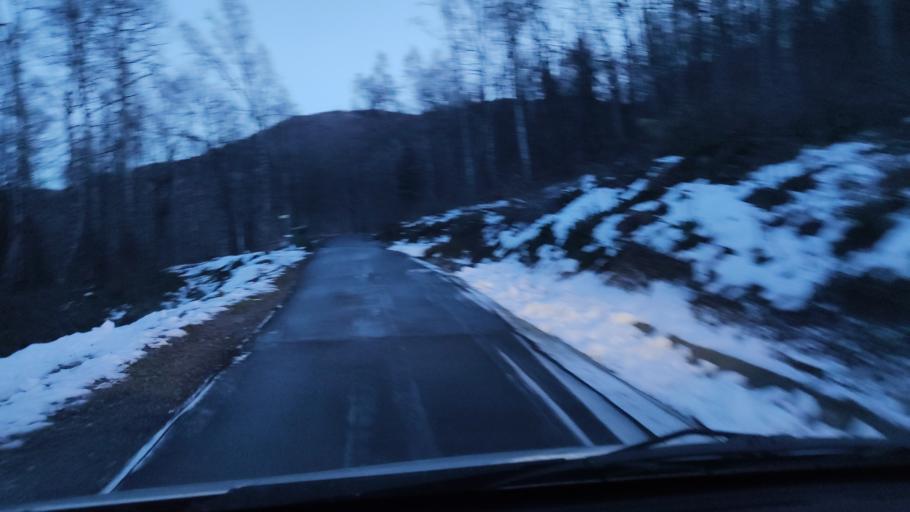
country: IT
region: Piedmont
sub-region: Provincia di Cuneo
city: Viola
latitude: 44.2752
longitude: 7.9677
